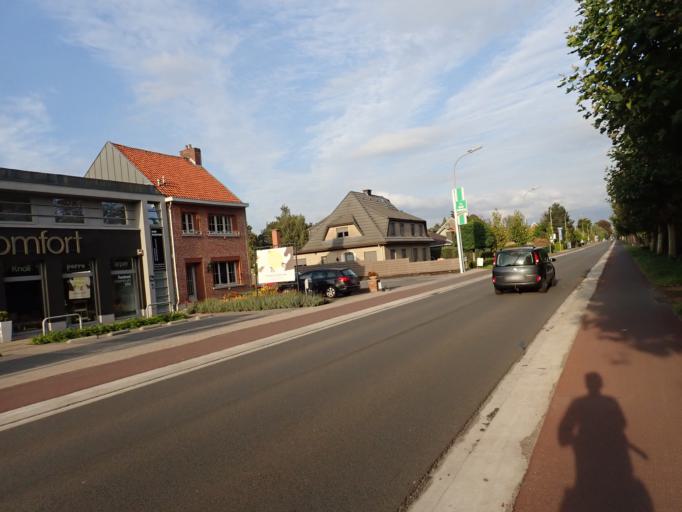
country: BE
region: Flanders
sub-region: Provincie Oost-Vlaanderen
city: Sint-Niklaas
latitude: 51.1728
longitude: 4.1663
